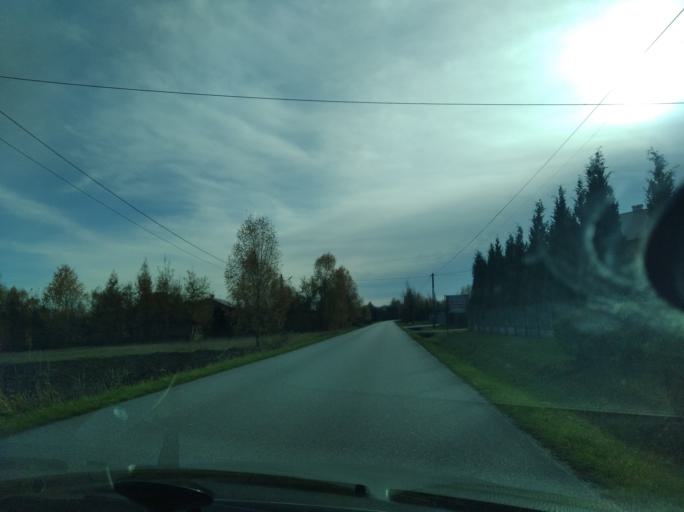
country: PL
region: Subcarpathian Voivodeship
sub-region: Powiat lancucki
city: Kraczkowa
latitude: 50.0400
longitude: 22.1357
